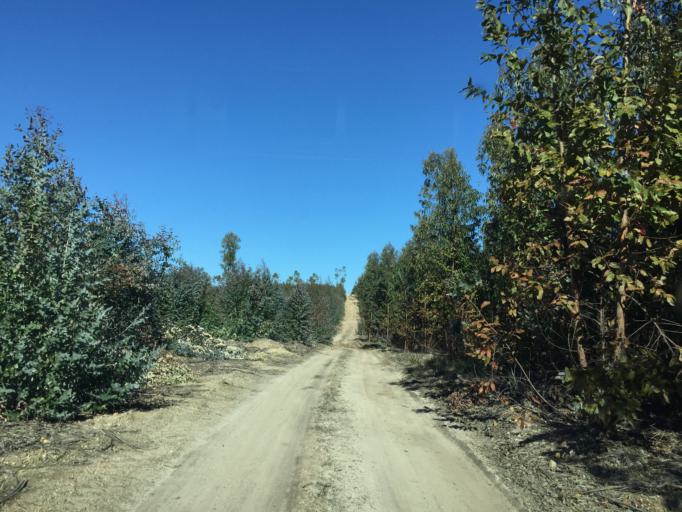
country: PT
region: Portalegre
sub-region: Nisa
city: Nisa
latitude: 39.4902
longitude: -7.7717
